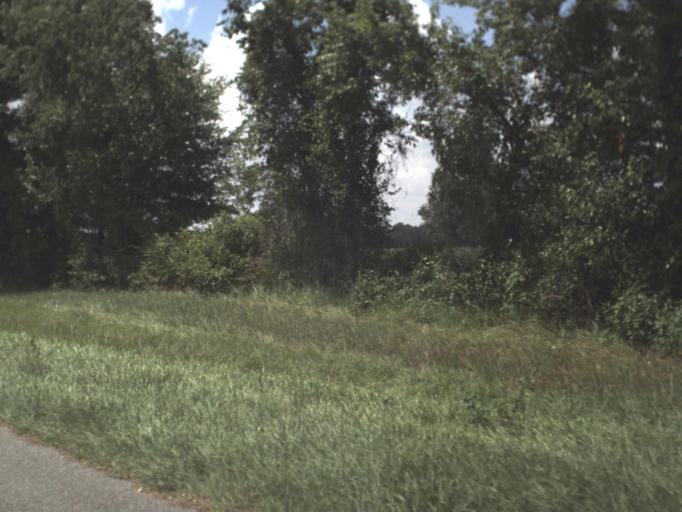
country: US
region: Florida
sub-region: Gilchrist County
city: Trenton
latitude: 29.6578
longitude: -82.8441
